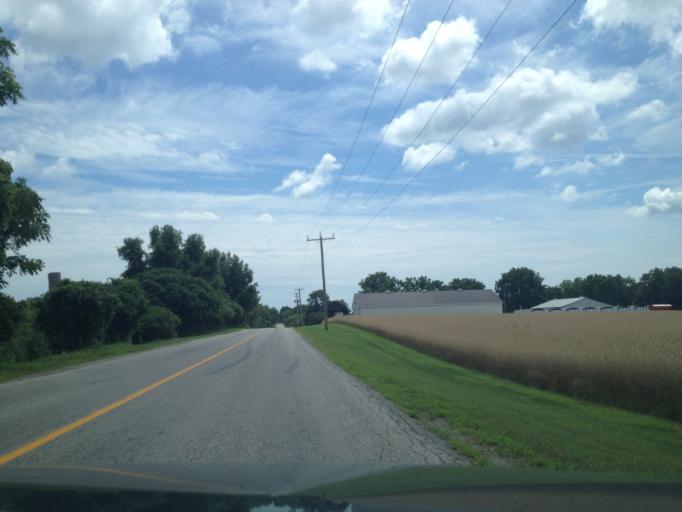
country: CA
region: Ontario
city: Norfolk County
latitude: 42.7840
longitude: -80.3007
